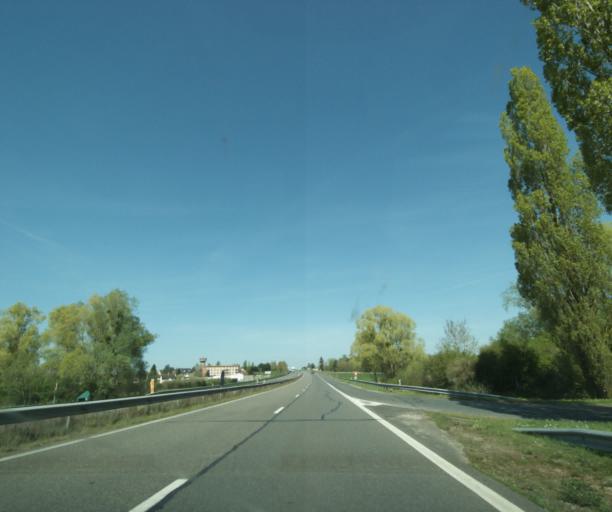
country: FR
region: Bourgogne
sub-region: Departement de la Nievre
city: Saint-Pierre-le-Moutier
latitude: 46.7908
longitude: 3.1250
